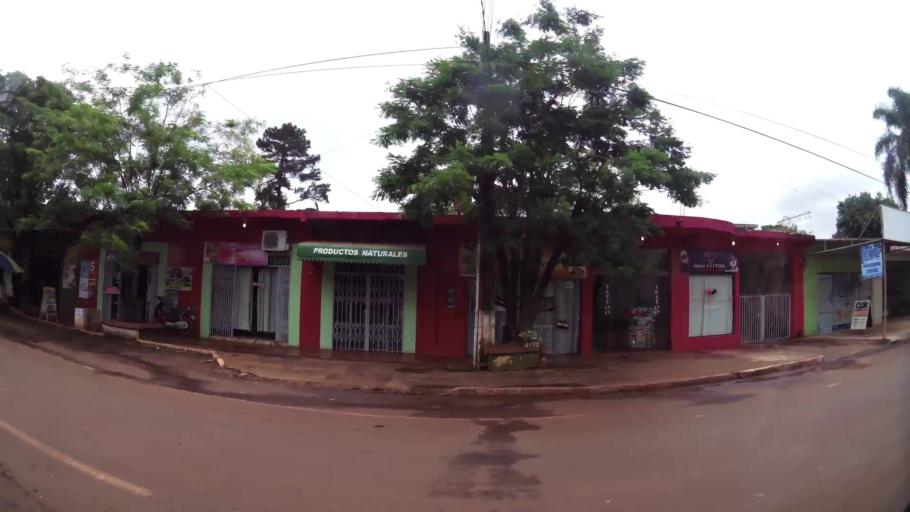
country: PY
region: Alto Parana
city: Ciudad del Este
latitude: -25.4831
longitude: -54.7623
